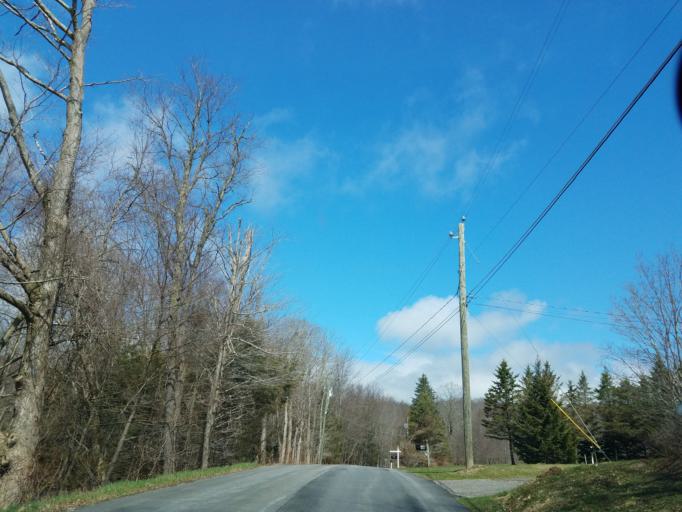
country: US
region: Connecticut
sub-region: Litchfield County
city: West Torrington
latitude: 41.7834
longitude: -73.1647
